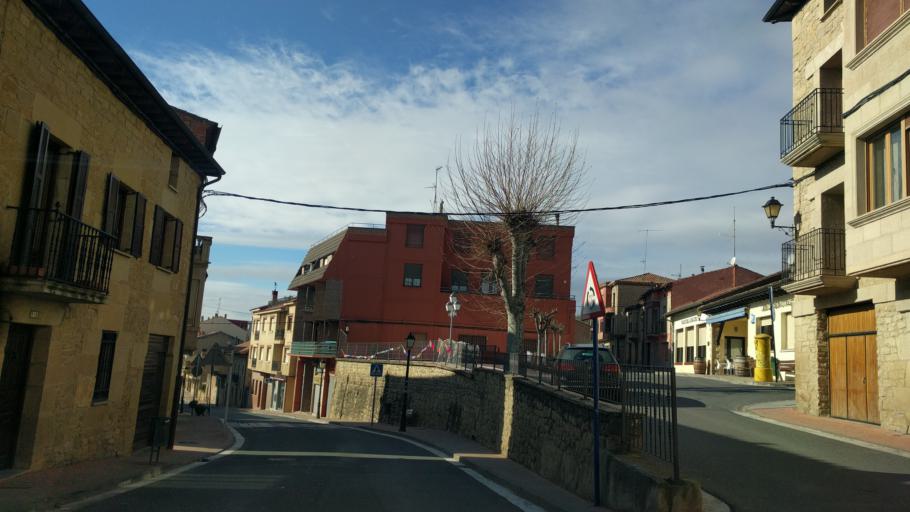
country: ES
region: Basque Country
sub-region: Provincia de Alava
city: Lapuebla de Labarca
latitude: 42.4935
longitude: -2.5741
